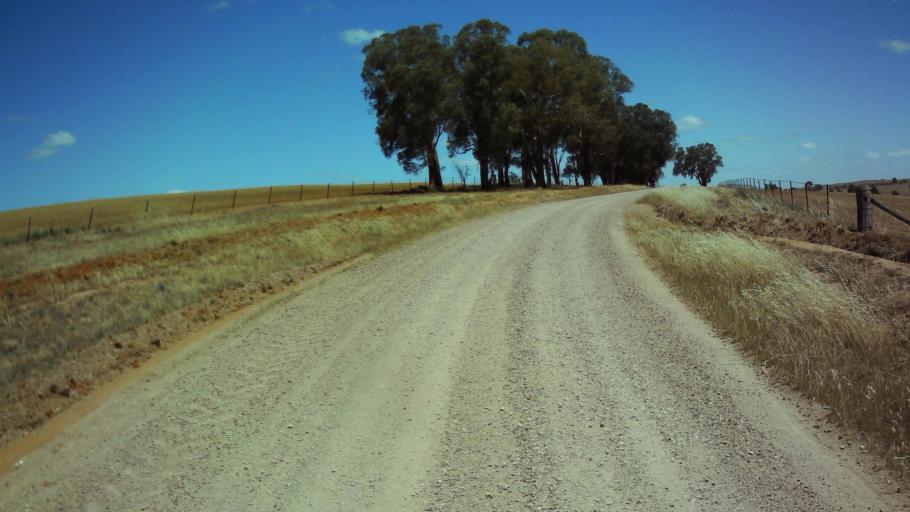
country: AU
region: New South Wales
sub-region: Weddin
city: Grenfell
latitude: -33.9404
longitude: 148.3298
